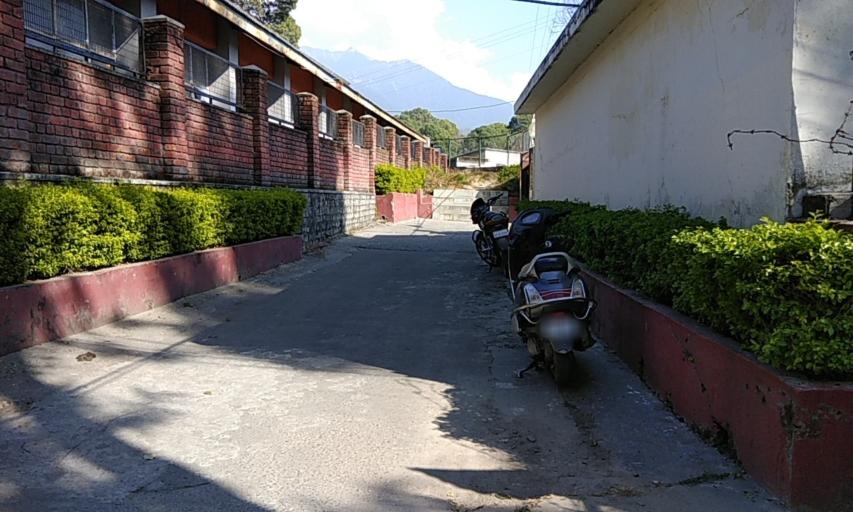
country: IN
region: Himachal Pradesh
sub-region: Kangra
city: Palampur
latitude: 32.1108
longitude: 76.5373
